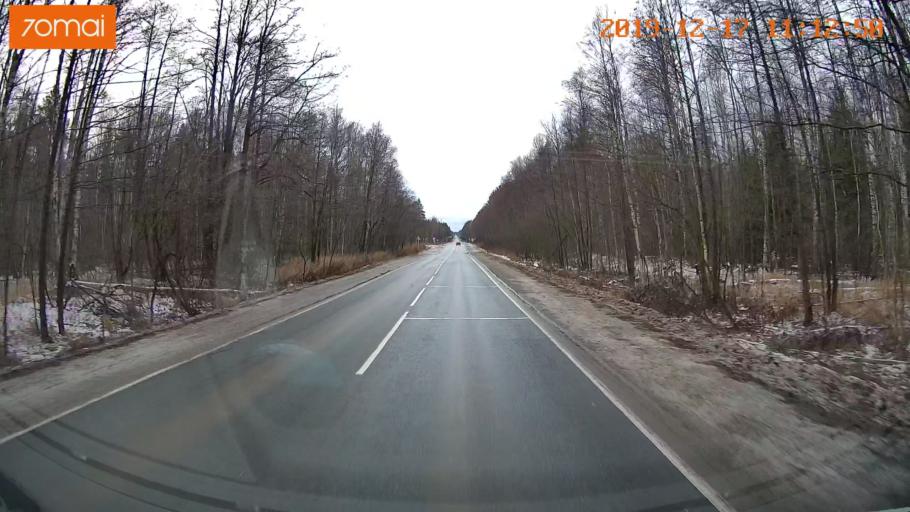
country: RU
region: Vladimir
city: Gus'-Khrustal'nyy
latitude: 55.5709
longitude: 40.6247
